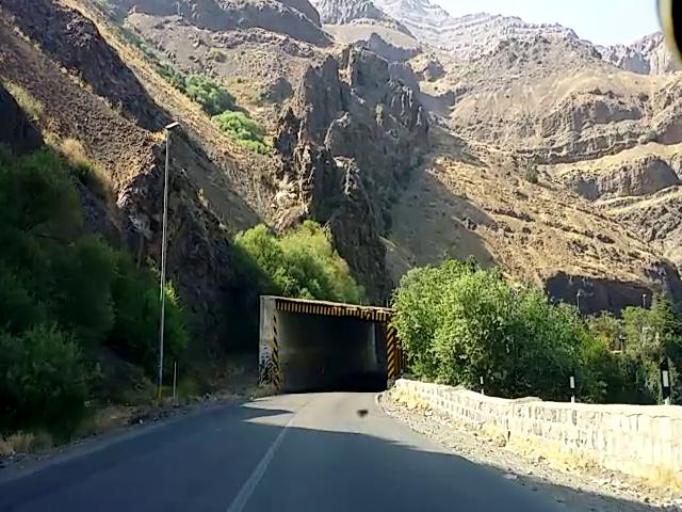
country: IR
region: Alborz
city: Karaj
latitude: 36.0000
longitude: 51.1137
